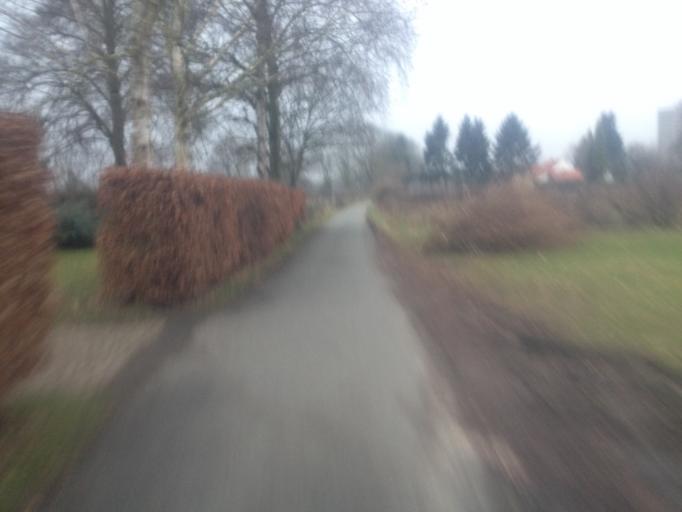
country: NL
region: Gelderland
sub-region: Gemeente Wageningen
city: Wageningen
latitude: 51.9774
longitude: 5.6863
